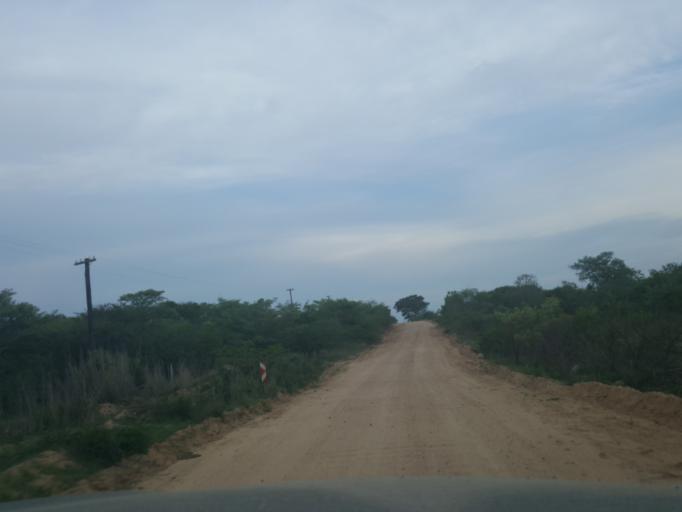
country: ZA
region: Limpopo
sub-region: Mopani District Municipality
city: Hoedspruit
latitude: -24.5622
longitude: 31.0172
